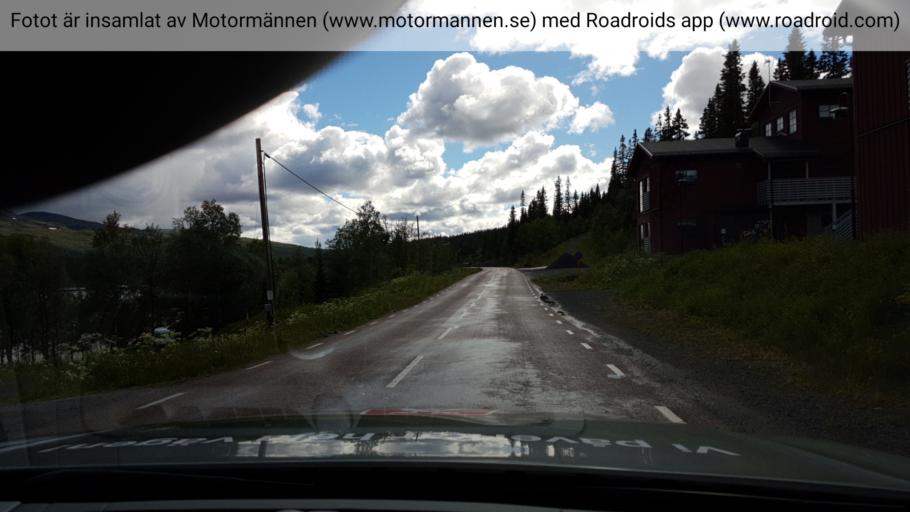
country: SE
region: Jaemtland
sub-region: Are Kommun
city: Jarpen
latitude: 63.1014
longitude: 13.7969
